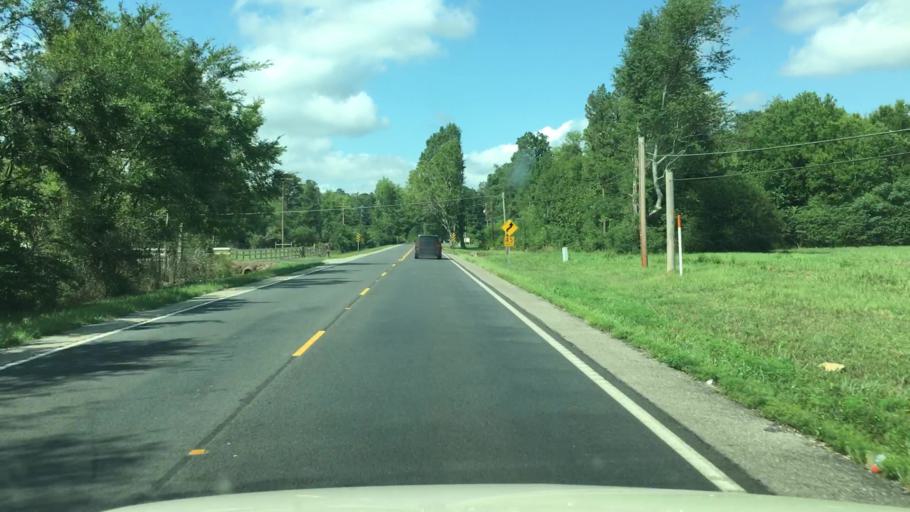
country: US
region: Arkansas
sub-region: Garland County
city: Lake Hamilton
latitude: 34.3980
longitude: -93.1024
